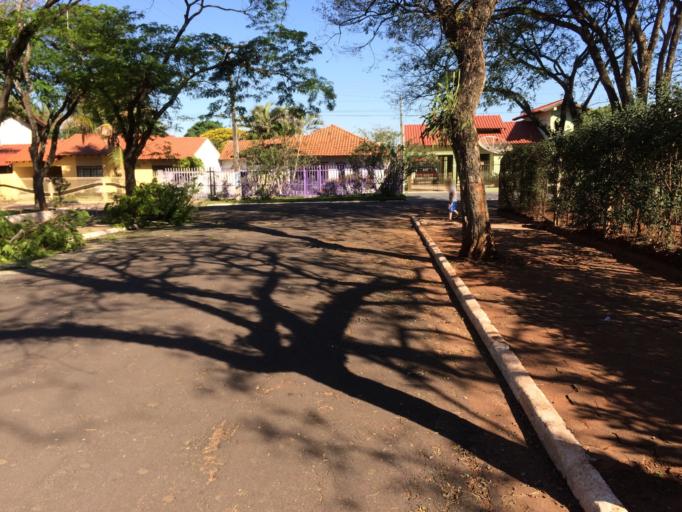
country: BR
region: Parana
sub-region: Cianorte
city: Cianorte
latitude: -23.5378
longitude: -52.5912
